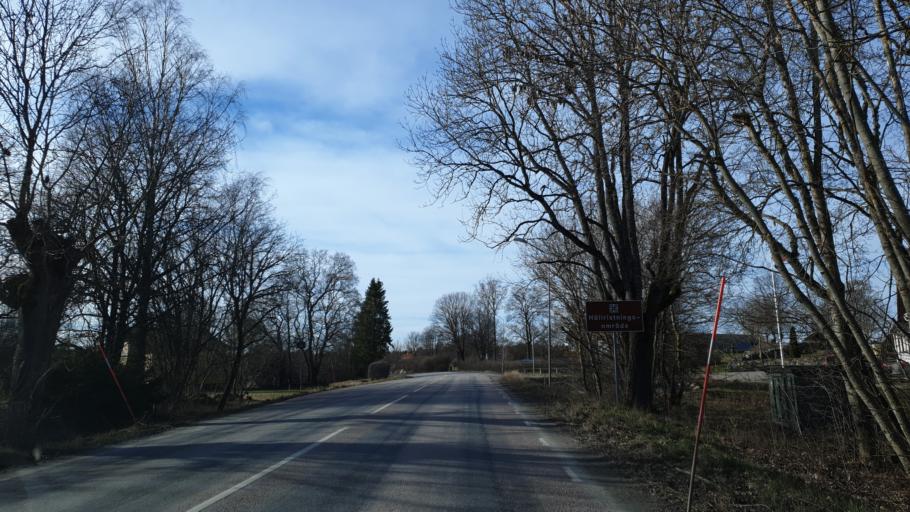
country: SE
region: Uppsala
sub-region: Enkopings Kommun
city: Grillby
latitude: 59.5950
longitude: 17.1780
